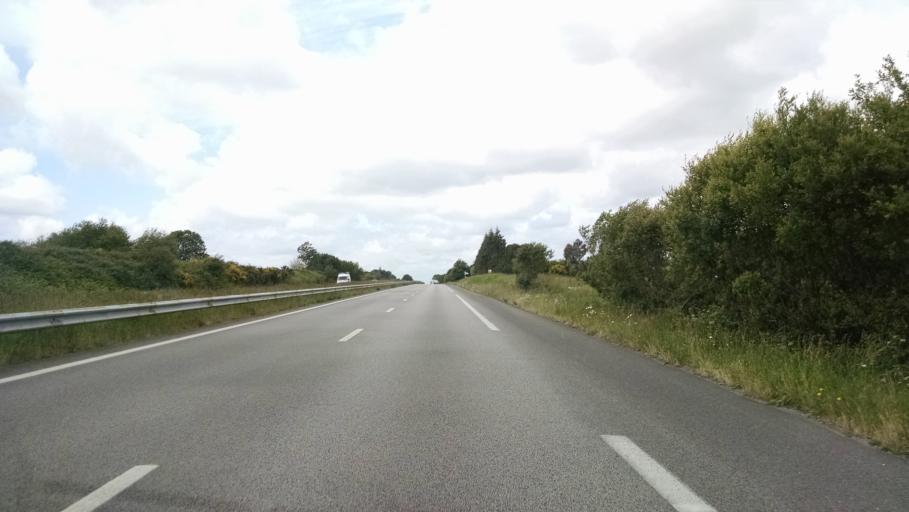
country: FR
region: Brittany
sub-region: Departement du Morbihan
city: Landaul
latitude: 47.7207
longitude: -3.0683
